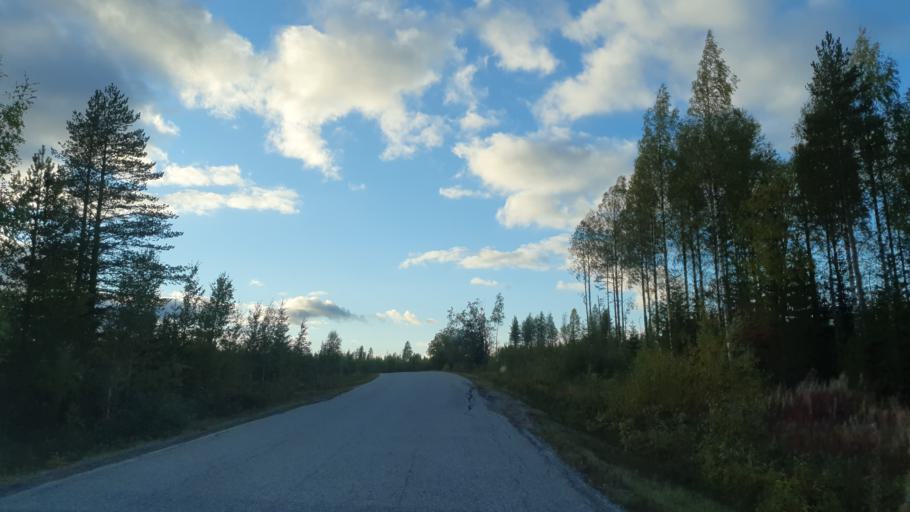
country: FI
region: Kainuu
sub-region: Kehys-Kainuu
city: Kuhmo
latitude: 63.9505
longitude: 29.7508
